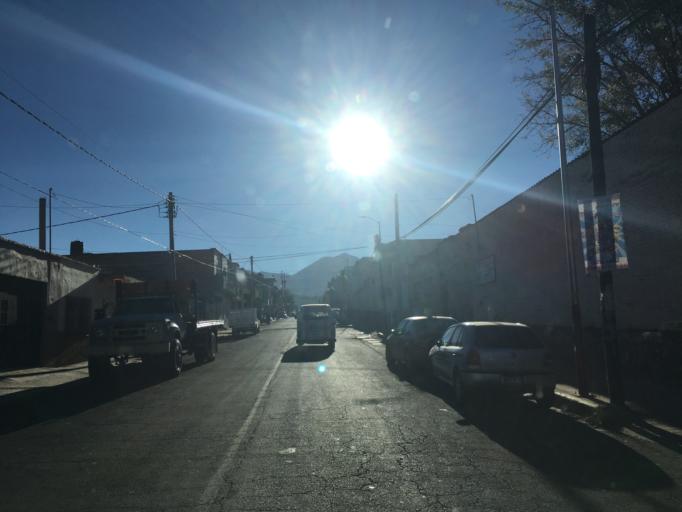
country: MX
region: Michoacan
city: Heroica Zitacuaro
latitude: 19.4405
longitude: -100.3538
